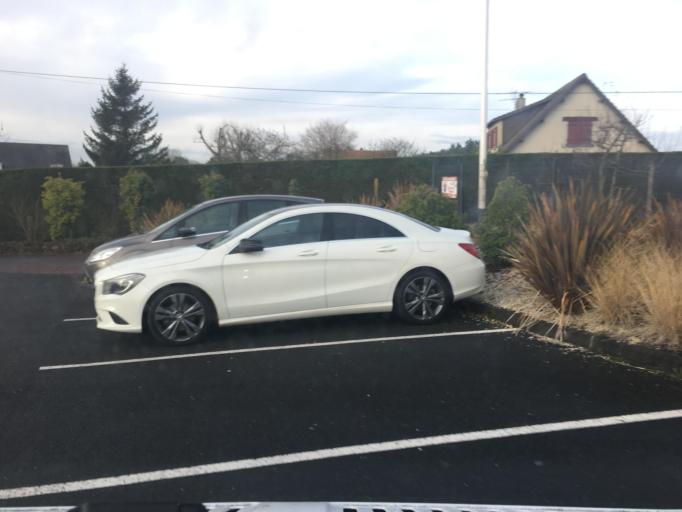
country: FR
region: Lower Normandy
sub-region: Departement du Calvados
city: Rots
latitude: 49.2026
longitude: -0.4632
